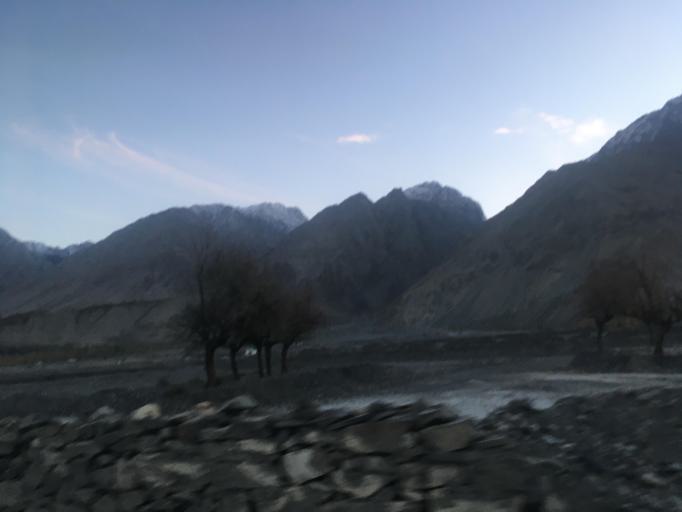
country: PK
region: Gilgit-Baltistan
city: Skardu
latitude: 35.3035
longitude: 75.5375
